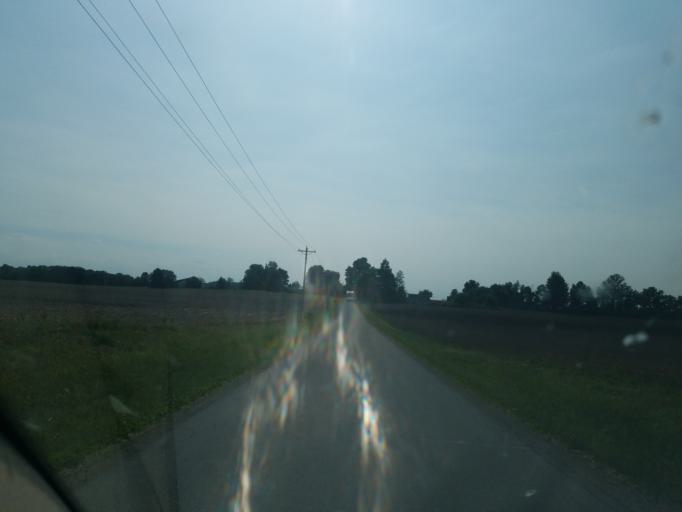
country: US
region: Ohio
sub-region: Wyandot County
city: Upper Sandusky
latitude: 40.9205
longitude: -83.1999
